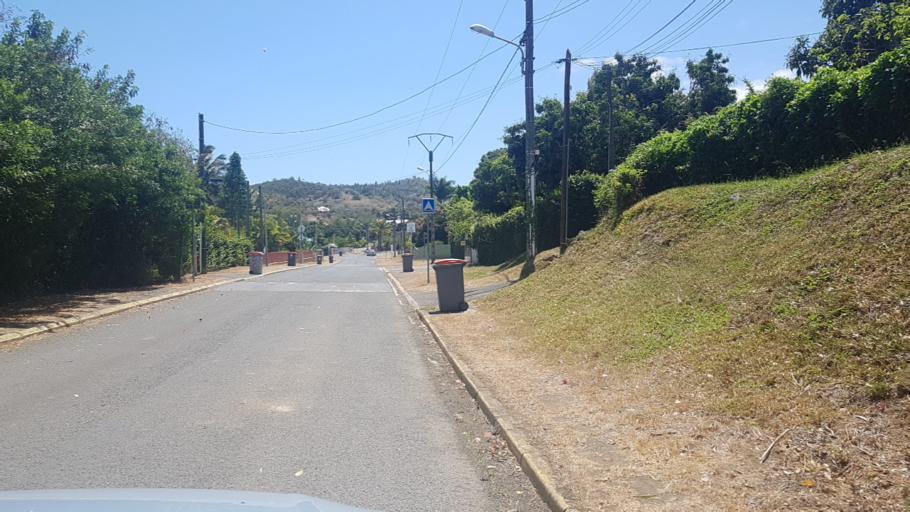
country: NC
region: South Province
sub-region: Dumbea
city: Dumbea
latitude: -22.1375
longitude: 166.4364
